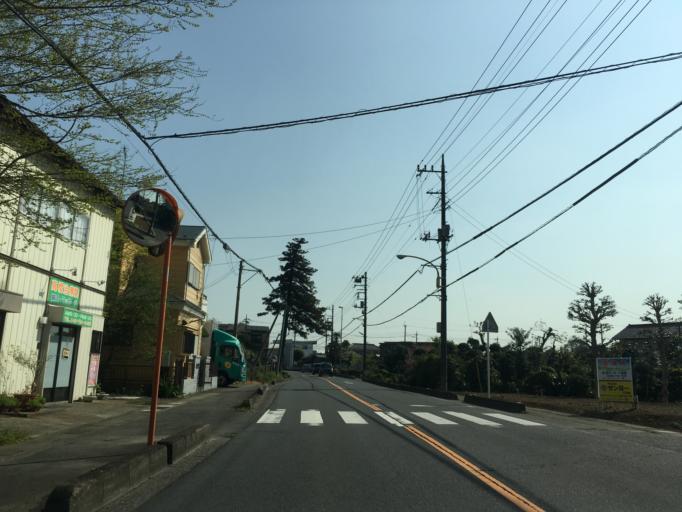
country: JP
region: Saitama
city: Shiraoka
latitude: 36.0014
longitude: 139.6957
